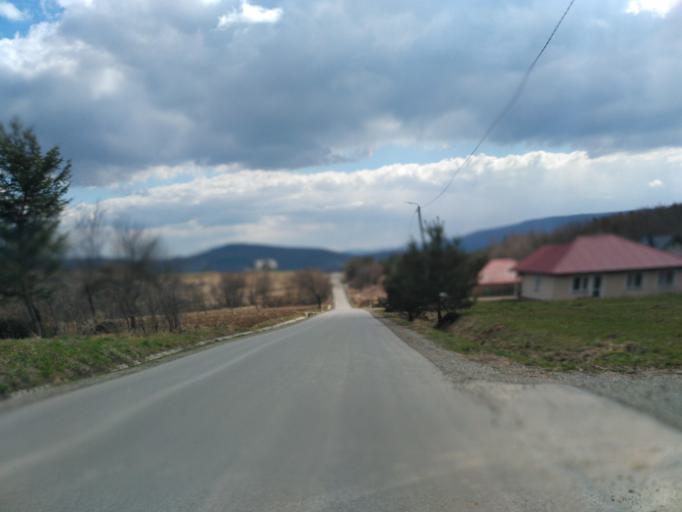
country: PL
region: Subcarpathian Voivodeship
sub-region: Powiat sanocki
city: Sanok
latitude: 49.6346
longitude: 22.2520
